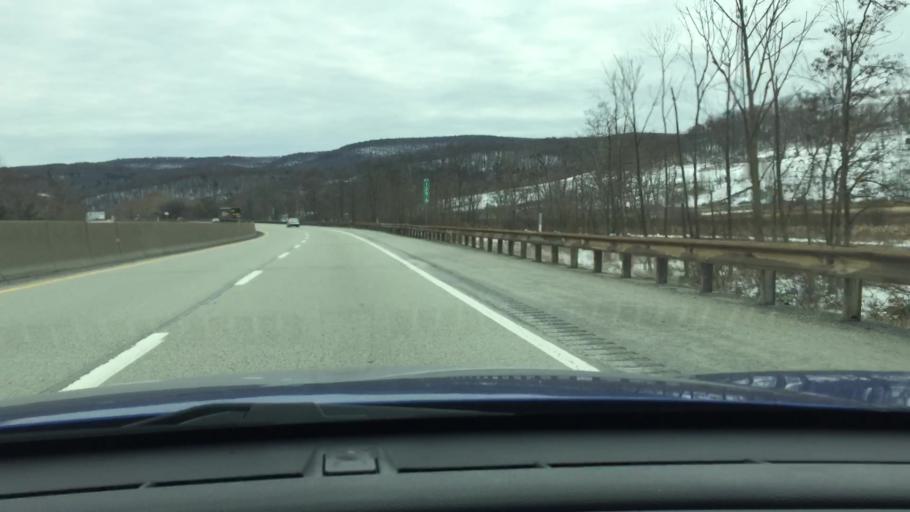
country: US
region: Pennsylvania
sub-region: Somerset County
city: Central City
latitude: 39.9788
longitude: -78.7650
